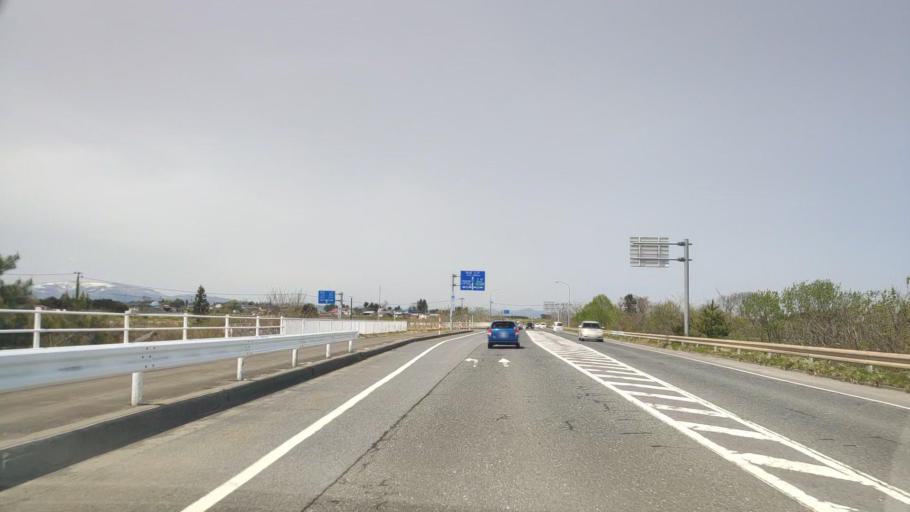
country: JP
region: Aomori
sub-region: Misawa Shi
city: Inuotose
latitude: 40.6323
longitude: 141.2468
